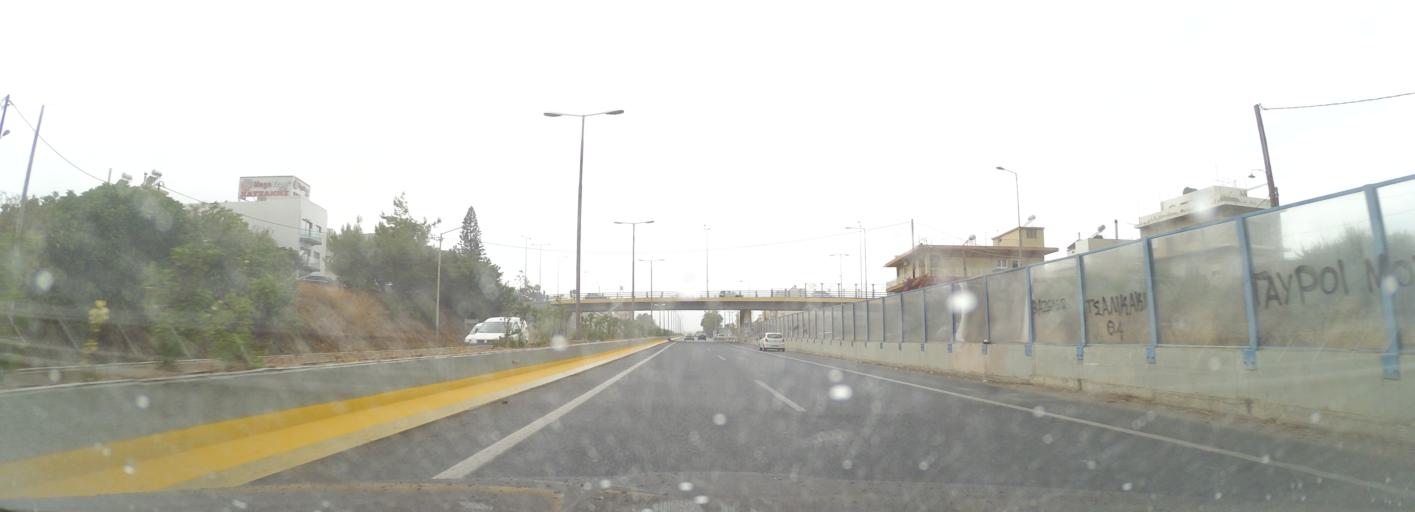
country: GR
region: Crete
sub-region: Nomos Irakleiou
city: Irakleion
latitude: 35.3199
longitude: 25.1407
